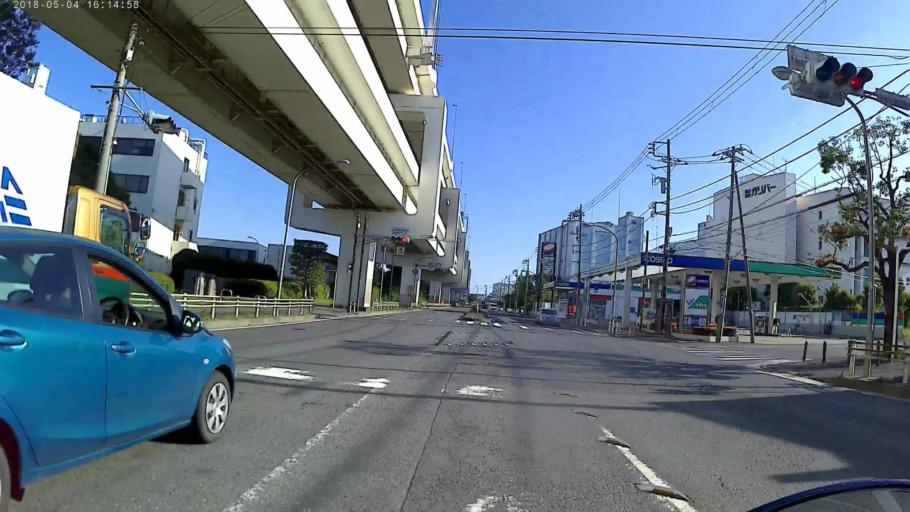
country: JP
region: Kanagawa
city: Yokohama
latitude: 35.4806
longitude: 139.6750
